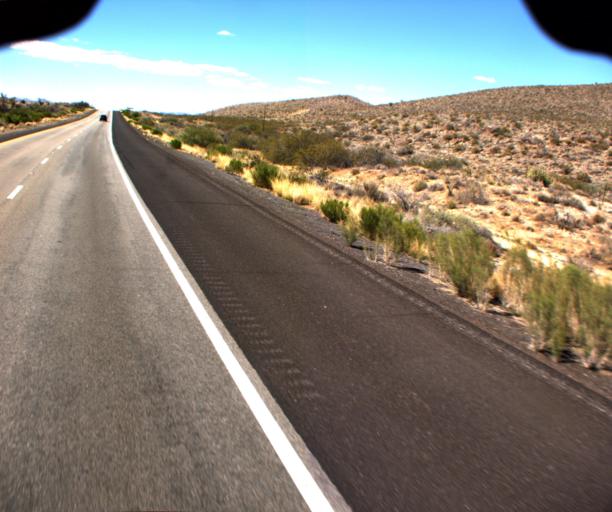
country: US
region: Arizona
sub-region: Mohave County
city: Kingman
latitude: 34.9504
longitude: -113.6679
